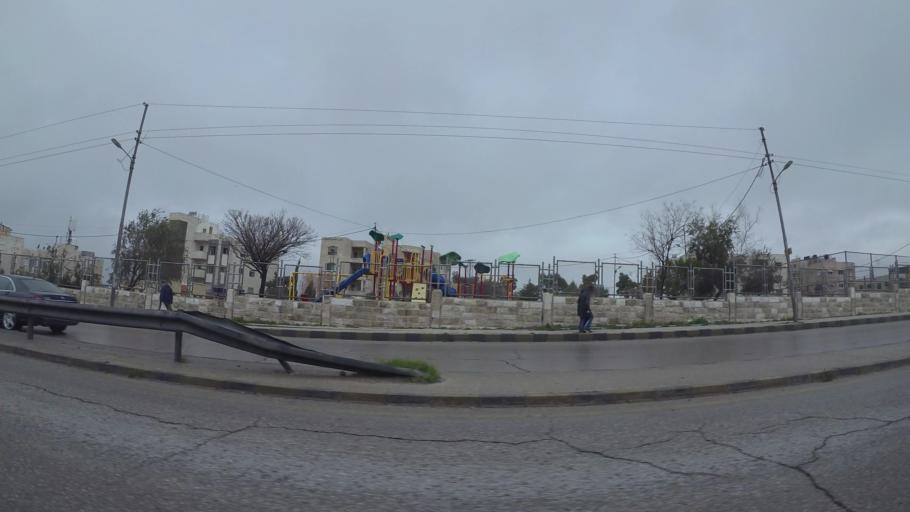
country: JO
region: Amman
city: Al Jubayhah
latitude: 32.0293
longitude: 35.8294
